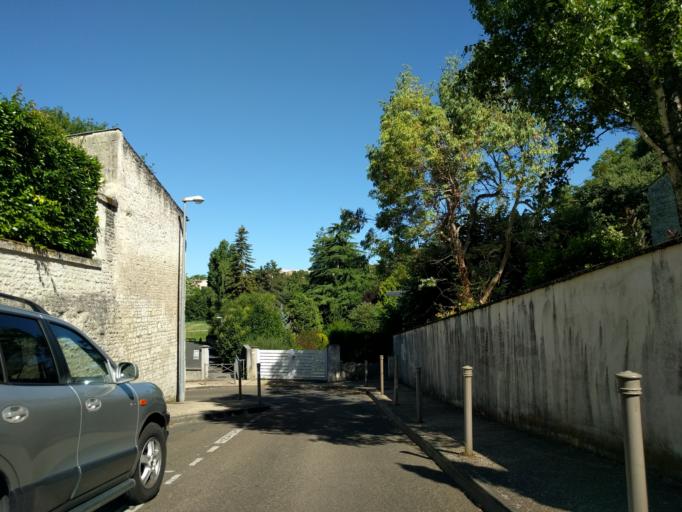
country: FR
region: Poitou-Charentes
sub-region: Departement des Deux-Sevres
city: Niort
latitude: 46.3269
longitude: -0.4507
